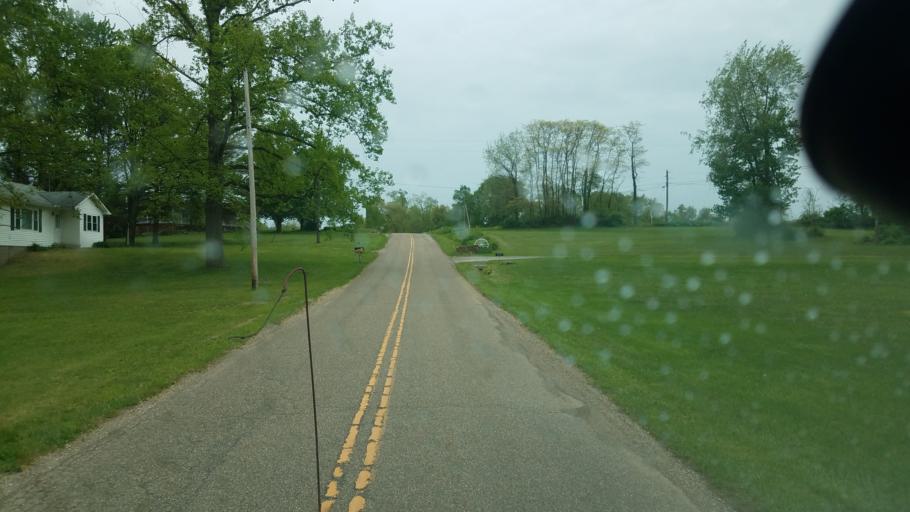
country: US
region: Ohio
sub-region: Guernsey County
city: Cambridge
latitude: 40.1451
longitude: -81.5368
